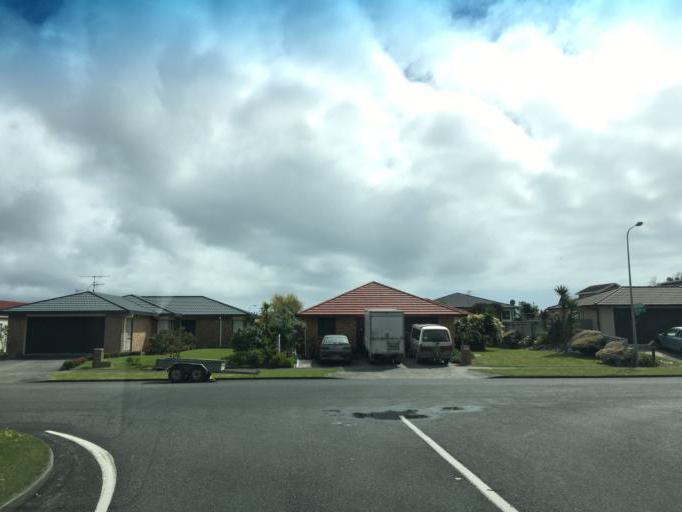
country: NZ
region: Wellington
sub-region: Kapiti Coast District
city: Paraparaumu
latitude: -40.8741
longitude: 175.0125
